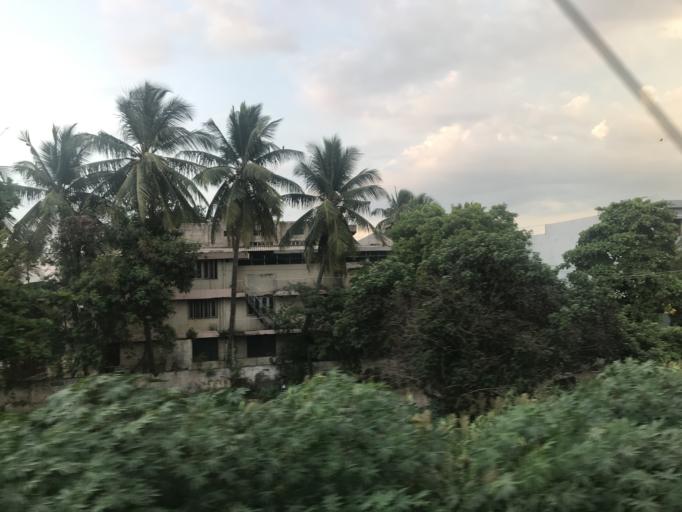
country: IN
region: Tamil Nadu
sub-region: Tiruppur
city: Tiruppur
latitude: 11.1106
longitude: 77.3469
